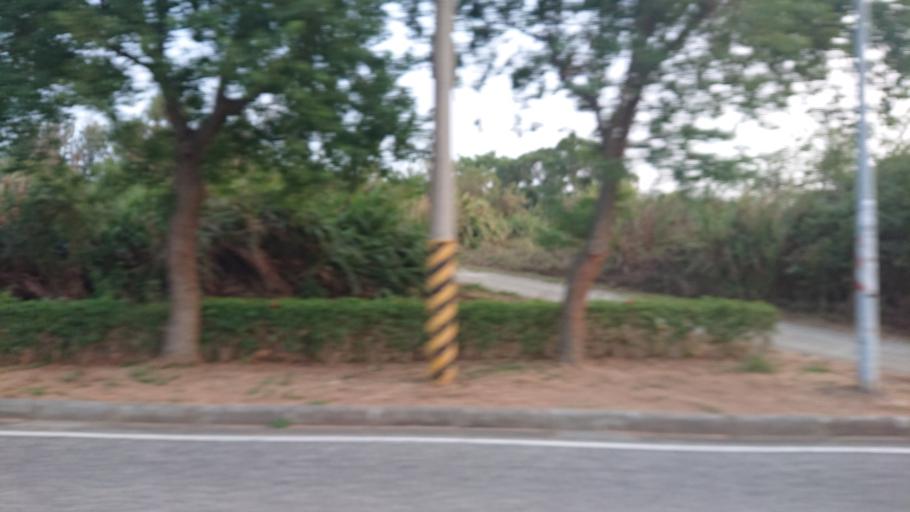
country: TW
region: Fukien
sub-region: Kinmen
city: Jincheng
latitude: 24.4681
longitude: 118.3949
